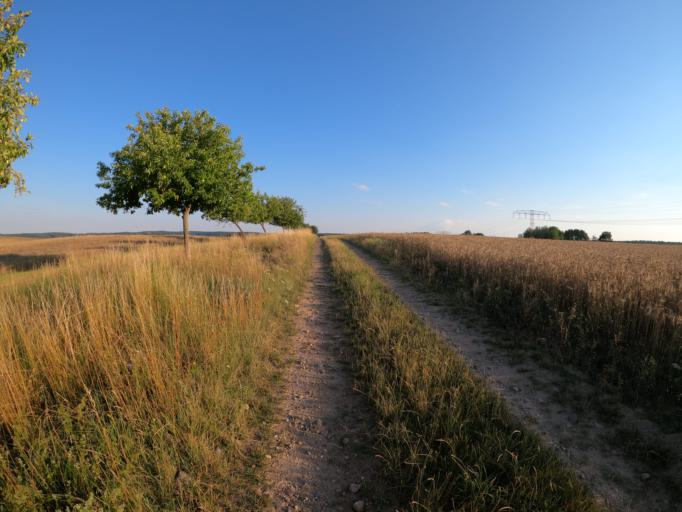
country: DE
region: Brandenburg
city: Althuttendorf
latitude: 53.0327
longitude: 13.8672
